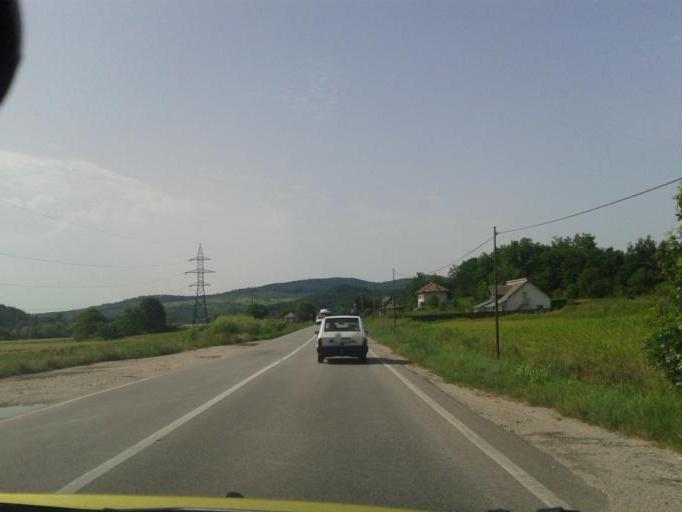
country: RO
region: Valcea
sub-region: Oras Baile Govora
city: Baile Govora
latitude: 45.0840
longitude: 24.2185
